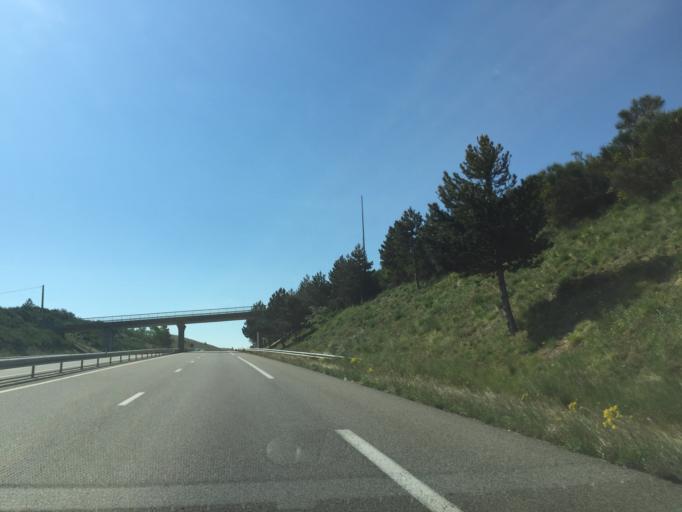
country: FR
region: Provence-Alpes-Cote d'Azur
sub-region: Departement des Alpes-de-Haute-Provence
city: Volonne
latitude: 44.1180
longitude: 5.9833
